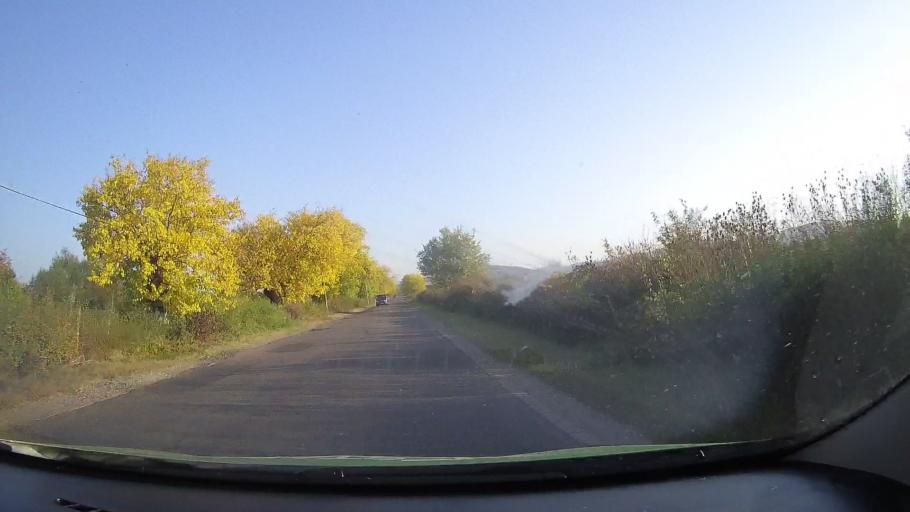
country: RO
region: Arad
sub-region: Comuna Pancota
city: Maderat
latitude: 46.3112
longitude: 21.7041
